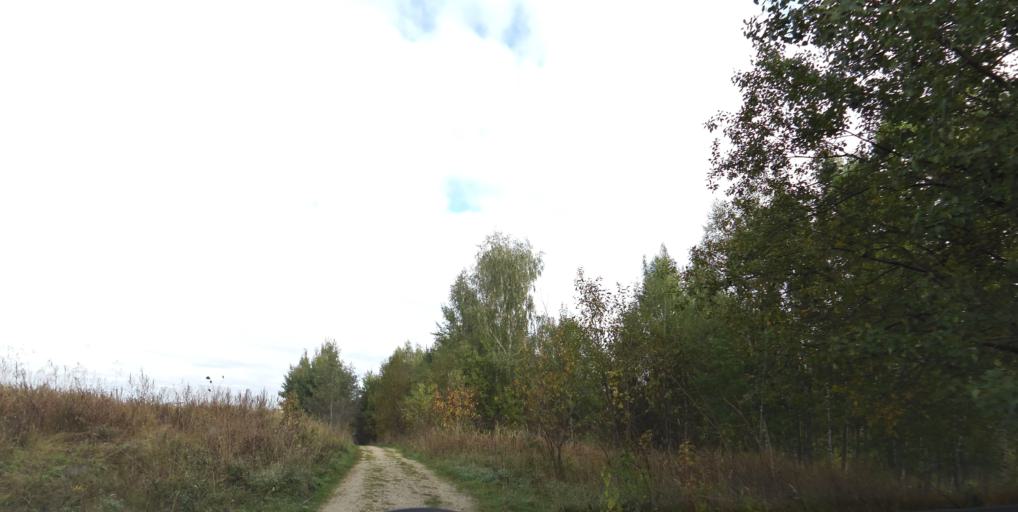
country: LT
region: Vilnius County
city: Justiniskes
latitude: 54.7140
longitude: 25.2094
